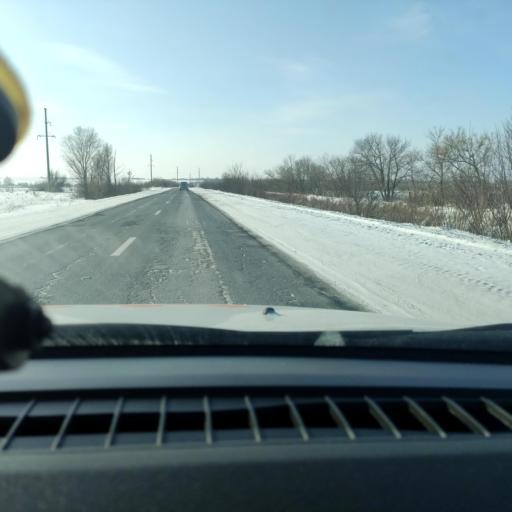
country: RU
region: Samara
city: Smyshlyayevka
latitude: 53.1551
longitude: 50.4309
